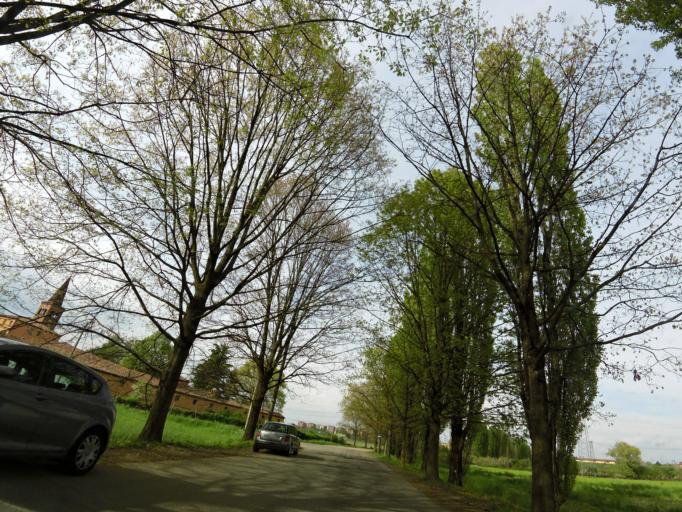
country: IT
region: Lombardy
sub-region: Citta metropolitana di Milano
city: San Giuliano Milanese
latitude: 45.3851
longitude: 9.2787
